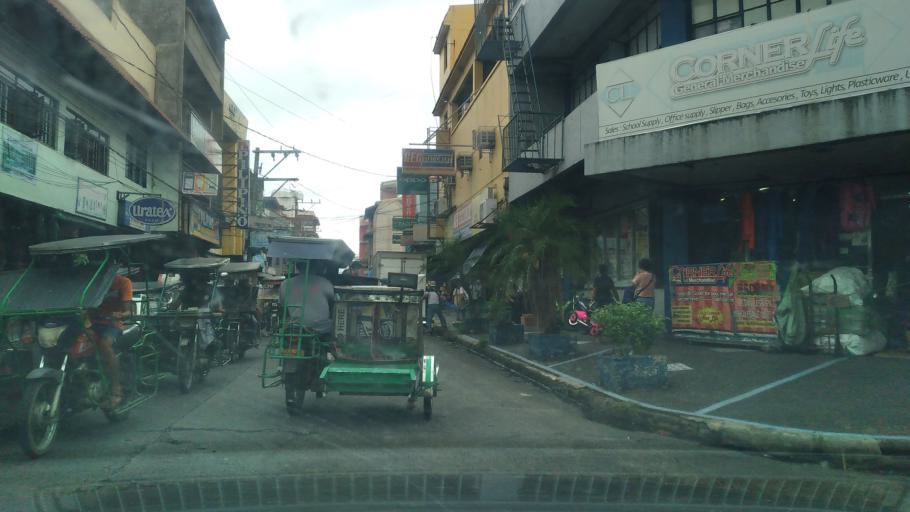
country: PH
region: Calabarzon
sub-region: Province of Quezon
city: Lucena
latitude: 13.9351
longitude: 121.6136
